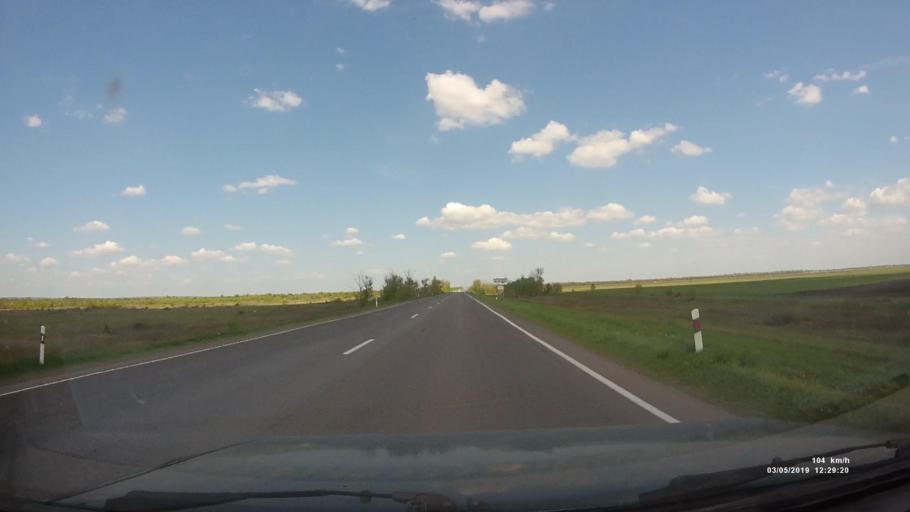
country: RU
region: Rostov
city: Semikarakorsk
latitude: 47.4861
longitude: 40.7348
